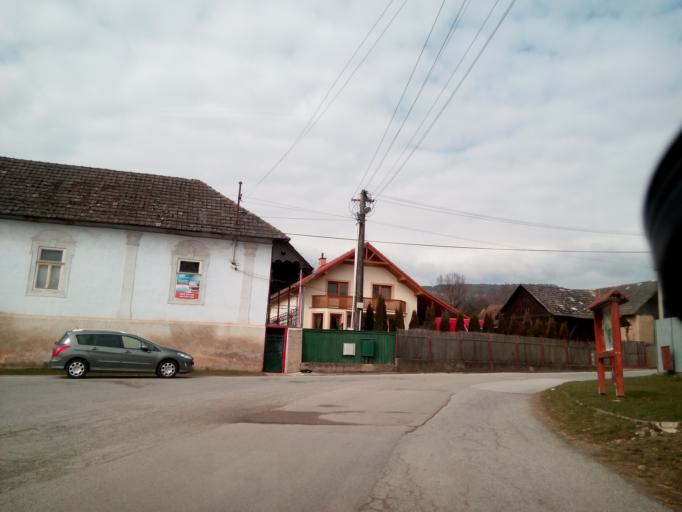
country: SK
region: Presovsky
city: Sabinov
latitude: 49.0473
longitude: 21.0169
